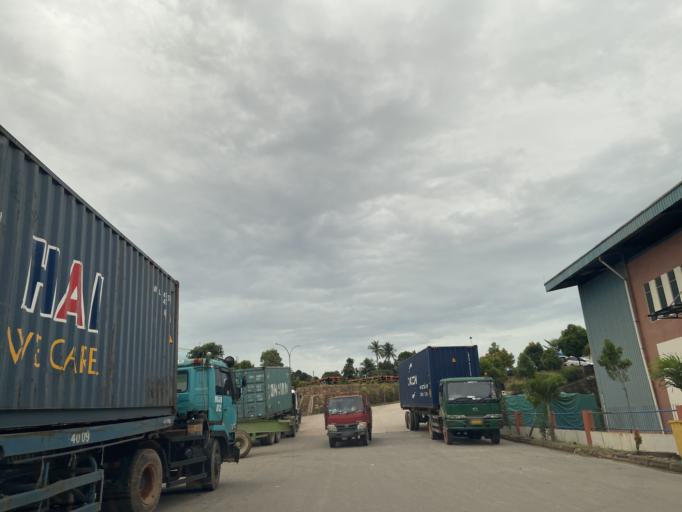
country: SG
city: Singapore
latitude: 1.1649
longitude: 104.0181
